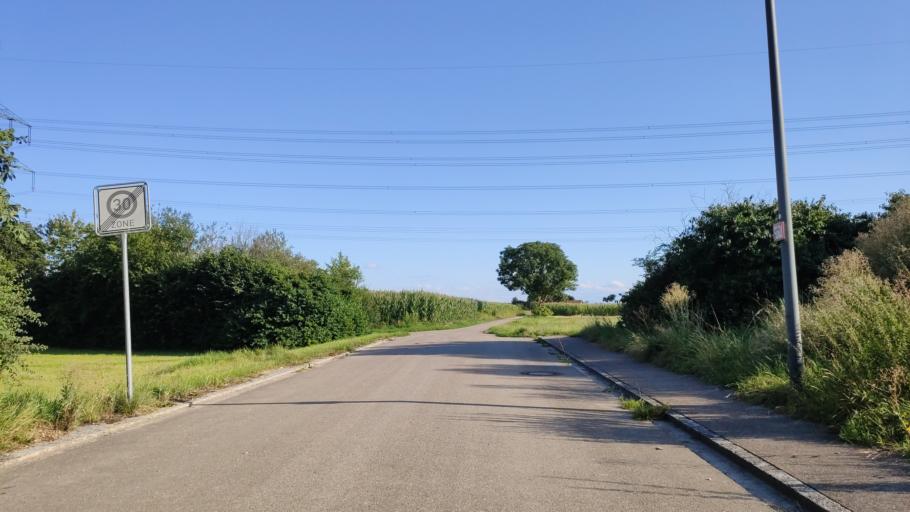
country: DE
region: Bavaria
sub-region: Swabia
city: Oberottmarshausen
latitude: 48.2327
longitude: 10.8585
